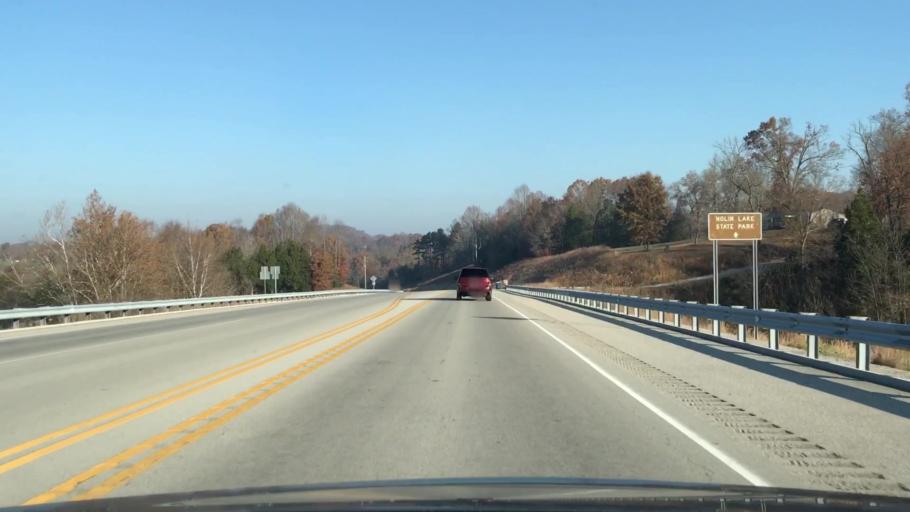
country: US
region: Kentucky
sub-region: Edmonson County
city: Brownsville
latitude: 37.1567
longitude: -86.2216
